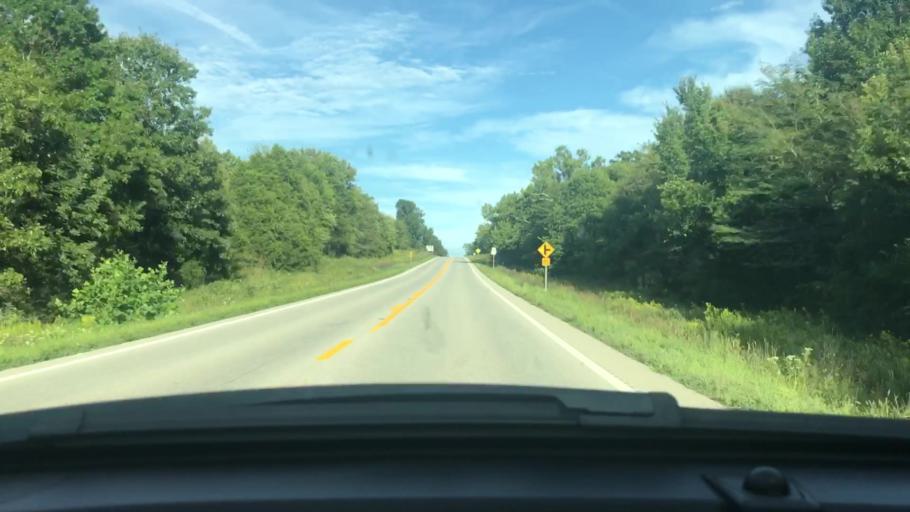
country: US
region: Arkansas
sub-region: Sharp County
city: Cherokee Village
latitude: 36.2745
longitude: -91.3454
